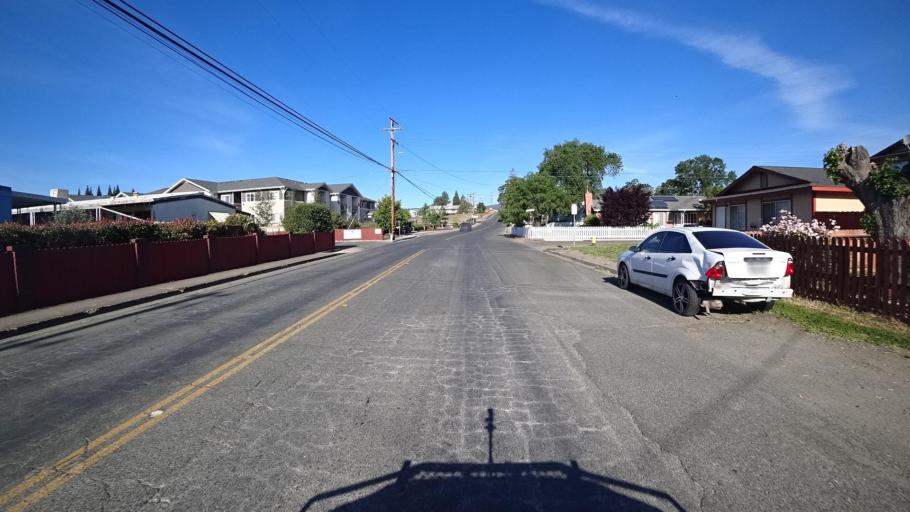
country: US
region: California
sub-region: Lake County
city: Lakeport
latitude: 39.0404
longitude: -122.9225
